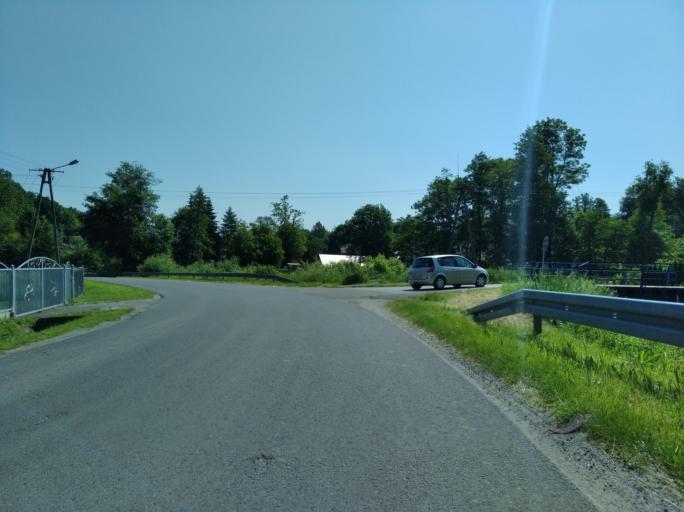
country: PL
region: Subcarpathian Voivodeship
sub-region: Powiat ropczycko-sedziszowski
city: Zagorzyce
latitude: 50.0092
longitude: 21.6622
